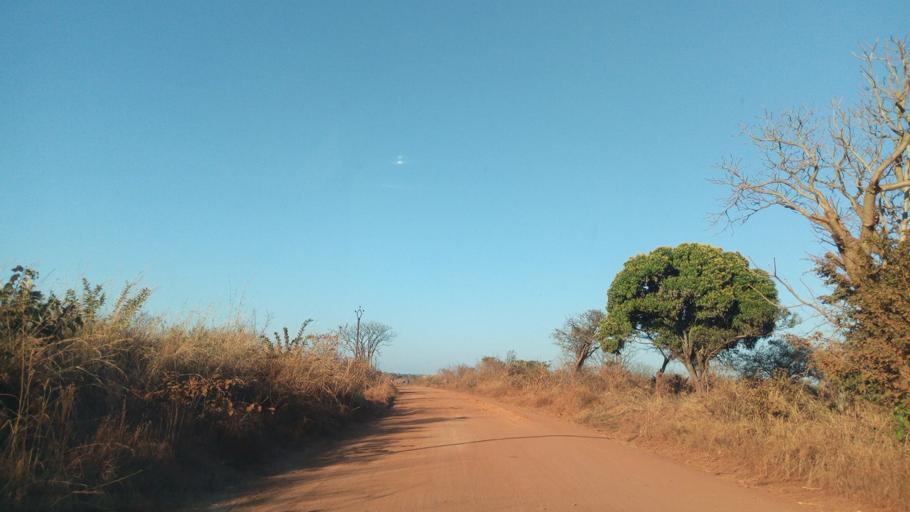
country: ZM
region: Luapula
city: Mwense
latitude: -10.4123
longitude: 28.6095
